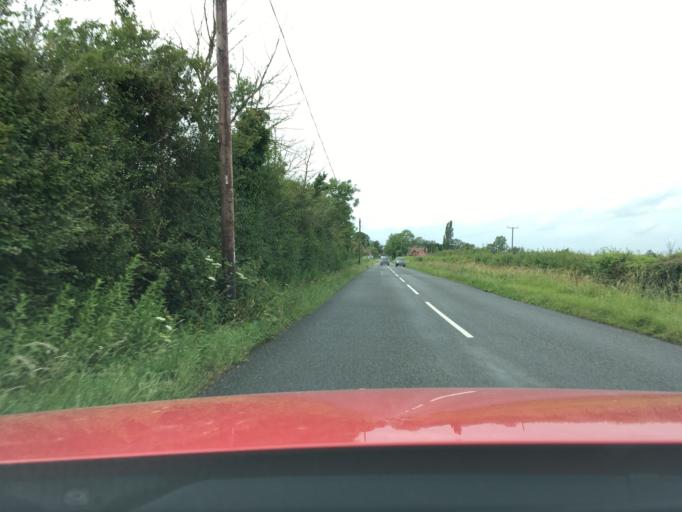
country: GB
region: England
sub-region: Worcestershire
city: Evesham
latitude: 52.0589
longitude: -1.9532
